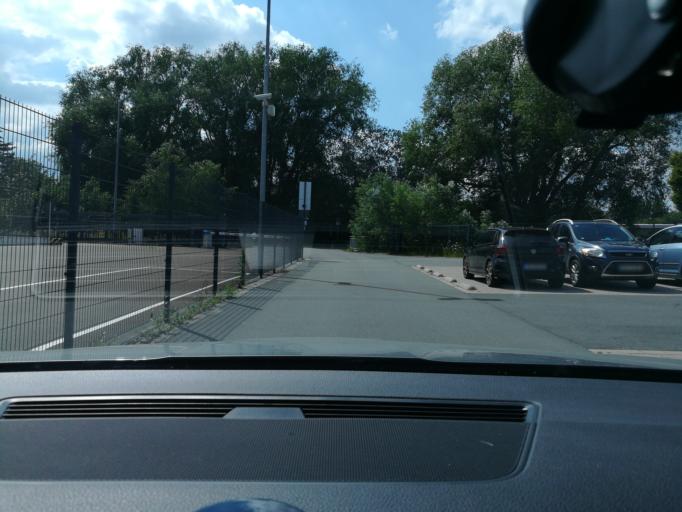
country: DE
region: North Rhine-Westphalia
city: Lubbecke
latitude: 52.3311
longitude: 8.6178
